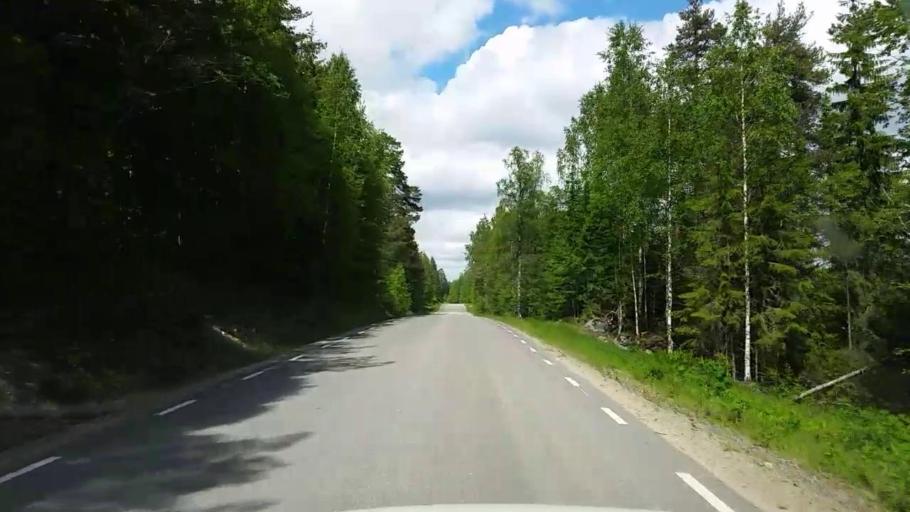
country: SE
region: Gaevleborg
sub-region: Bollnas Kommun
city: Vittsjo
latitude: 61.1012
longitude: 16.1606
